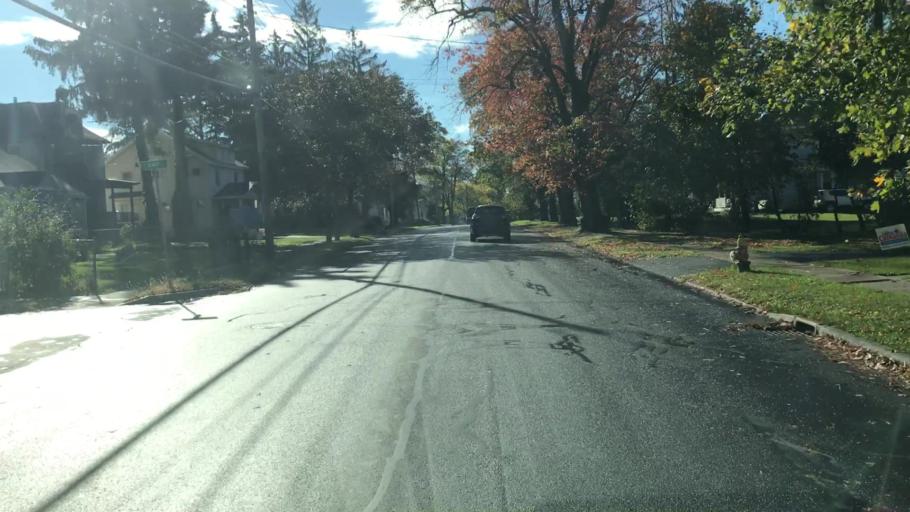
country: US
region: New York
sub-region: Cayuga County
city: Auburn
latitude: 42.9236
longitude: -76.5539
